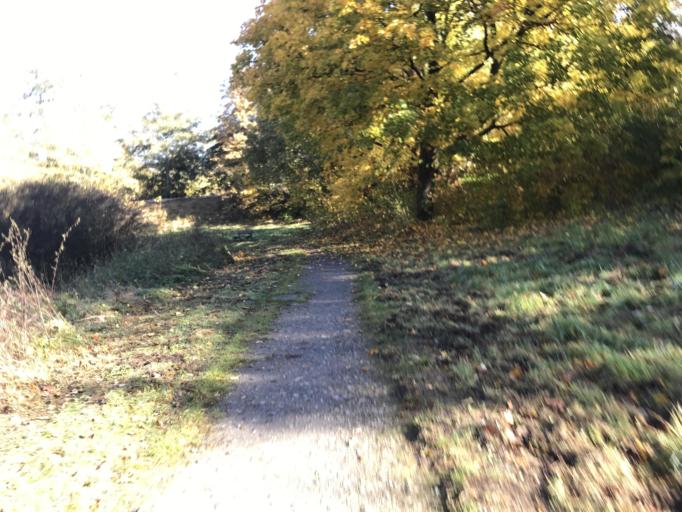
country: DE
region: Hesse
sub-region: Regierungsbezirk Giessen
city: Braunfels
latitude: 50.5248
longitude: 8.3835
